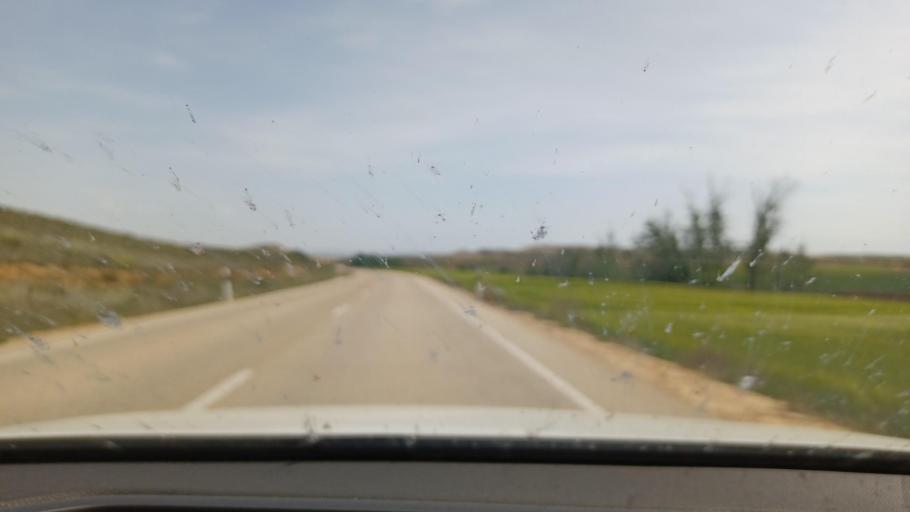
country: ES
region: Castille and Leon
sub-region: Provincia de Soria
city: Monteagudo de las Vicarias
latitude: 41.3865
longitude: -2.1937
